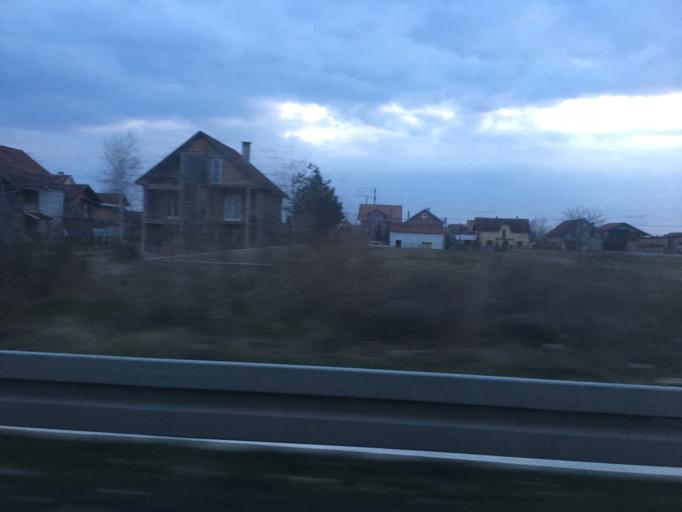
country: RS
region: Central Serbia
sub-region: Belgrade
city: Zemun
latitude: 44.8928
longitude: 20.4573
